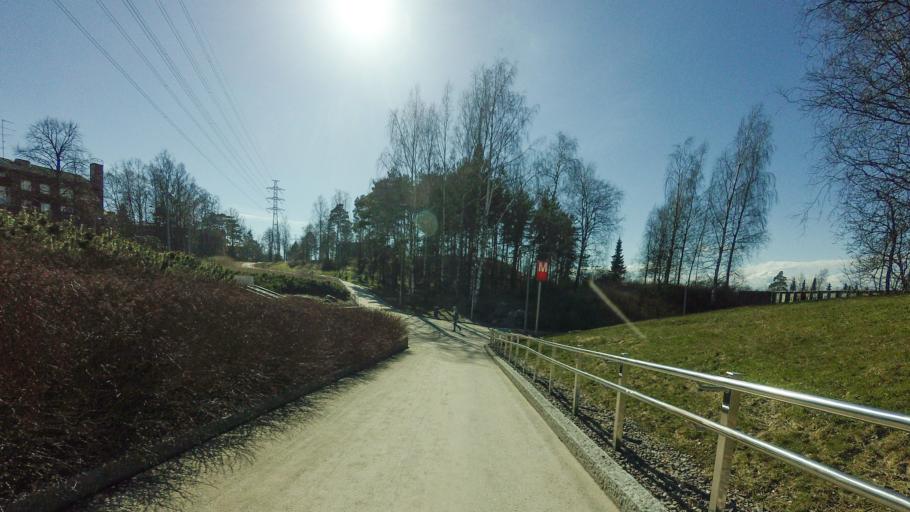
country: FI
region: Uusimaa
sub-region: Helsinki
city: Helsinki
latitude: 60.1881
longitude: 25.0075
